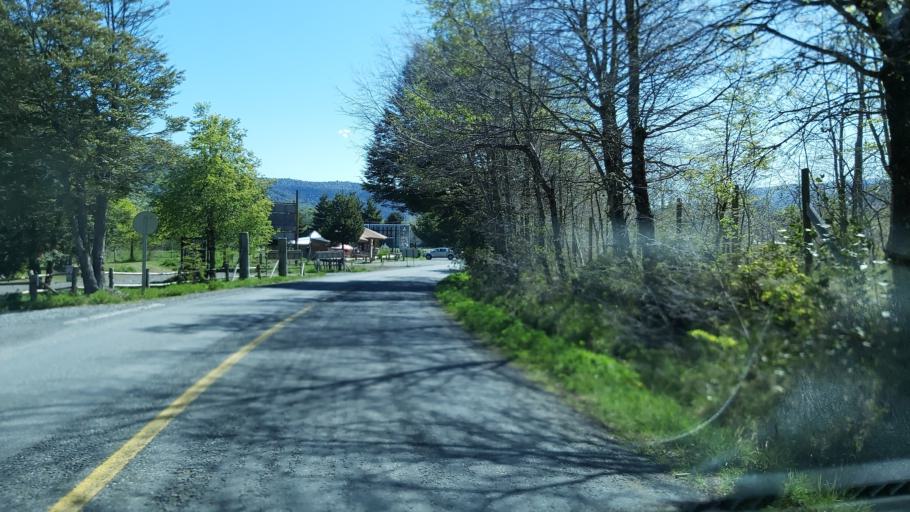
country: CL
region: Araucania
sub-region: Provincia de Cautin
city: Vilcun
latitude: -38.4783
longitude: -71.5349
